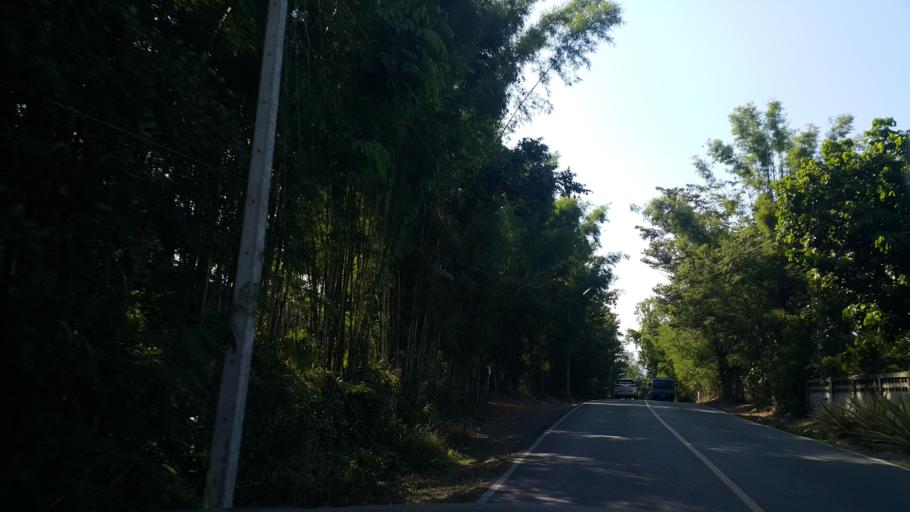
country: TH
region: Chiang Mai
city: San Sai
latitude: 18.9365
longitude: 98.9355
